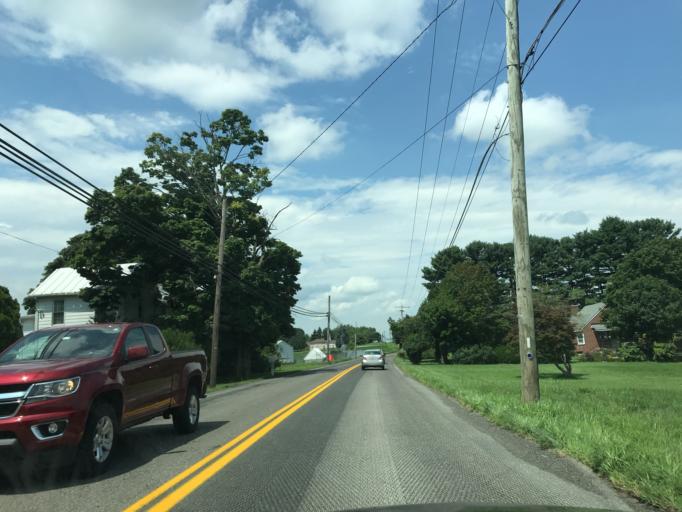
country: US
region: Pennsylvania
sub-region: York County
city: New Freedom
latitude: 39.6734
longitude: -76.7209
